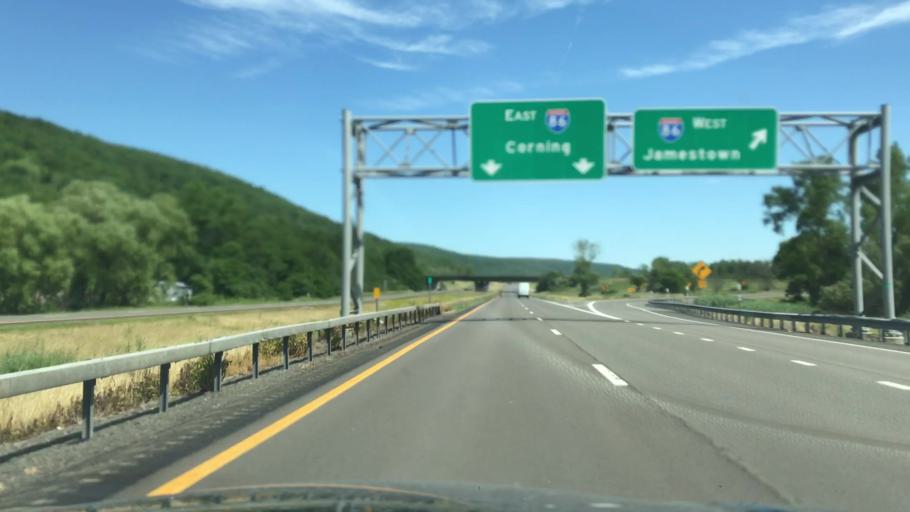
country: US
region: New York
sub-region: Steuben County
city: Bath
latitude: 42.3918
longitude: -77.3910
